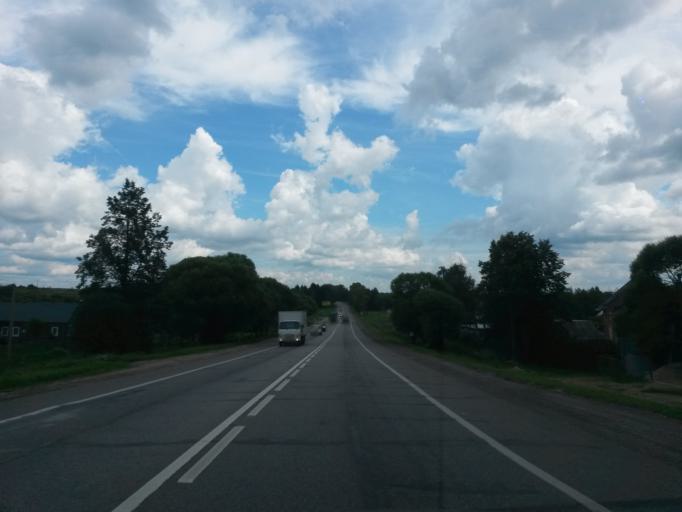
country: RU
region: Vladimir
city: Aleksandrov
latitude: 56.6040
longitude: 38.6311
